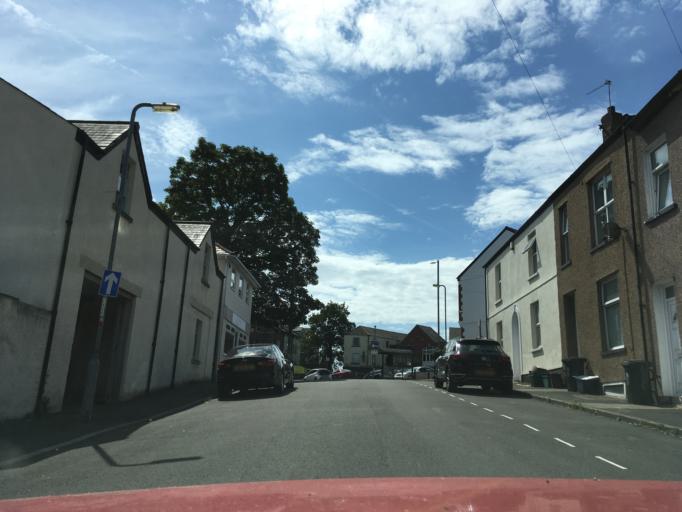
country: GB
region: Wales
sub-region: Newport
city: Newport
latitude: 51.5836
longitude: -3.0003
